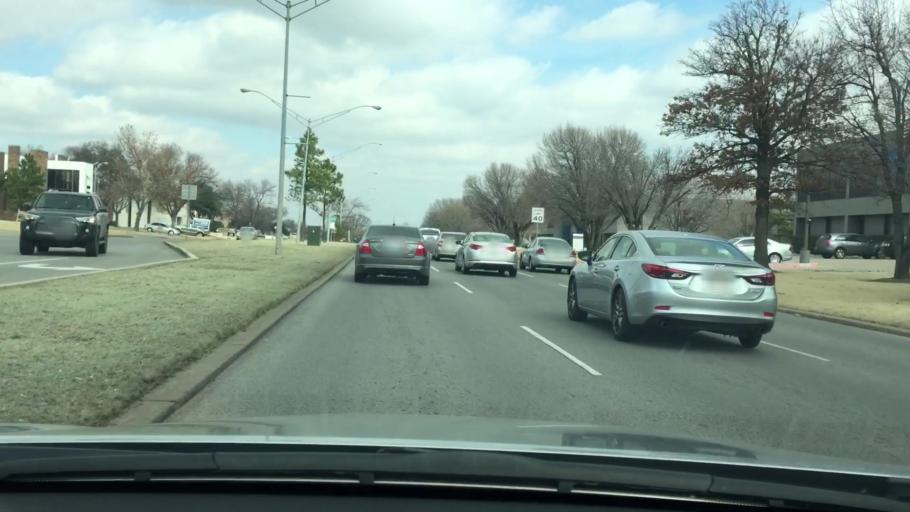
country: US
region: Oklahoma
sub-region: Oklahoma County
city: Oklahoma City
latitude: 35.5081
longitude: -97.5343
